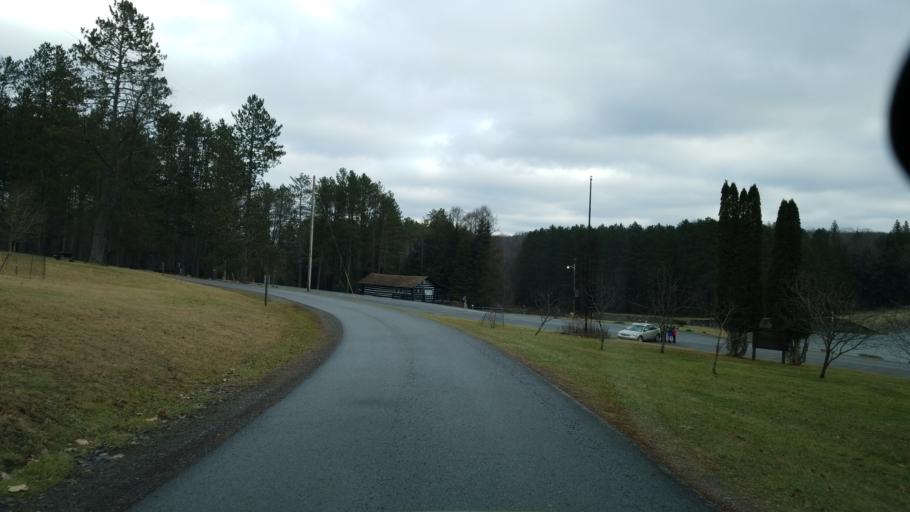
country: US
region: Pennsylvania
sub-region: Clearfield County
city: Clearfield
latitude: 41.1982
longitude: -78.5102
